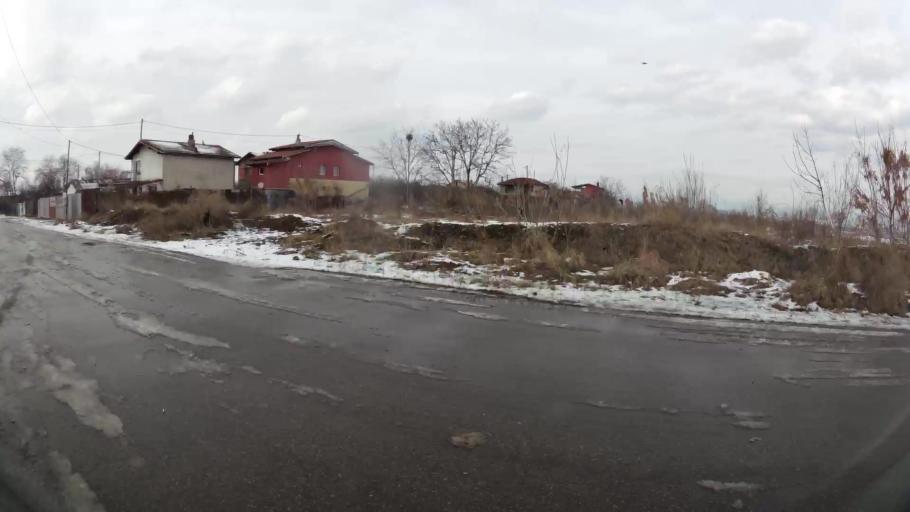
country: BG
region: Sofia-Capital
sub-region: Stolichna Obshtina
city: Sofia
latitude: 42.6914
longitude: 23.3883
